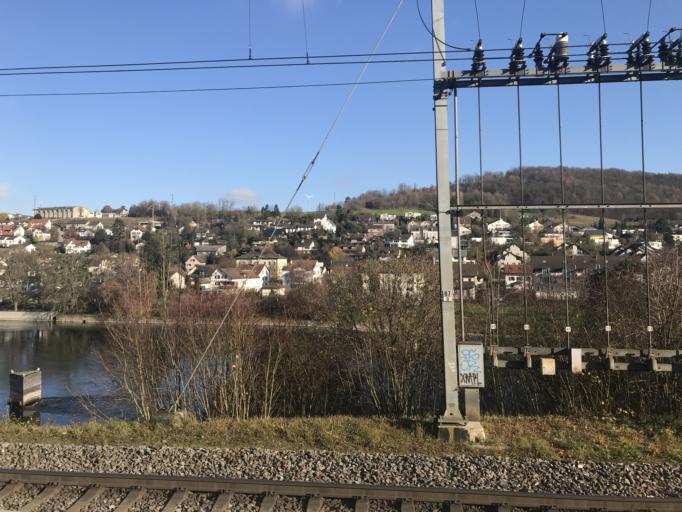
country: CH
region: Zurich
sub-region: Bezirk Andelfingen
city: Flurlingen
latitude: 47.6845
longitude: 8.6247
